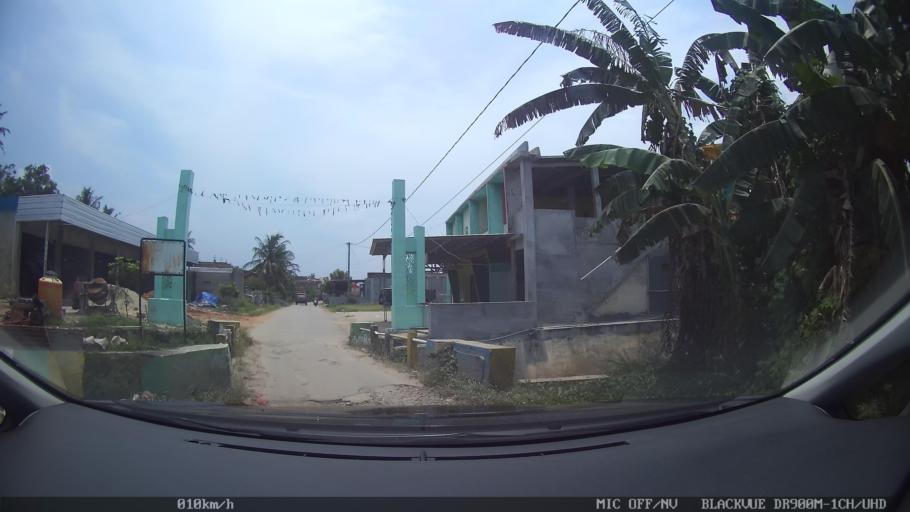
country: ID
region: Lampung
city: Kedaton
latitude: -5.3389
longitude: 105.2477
